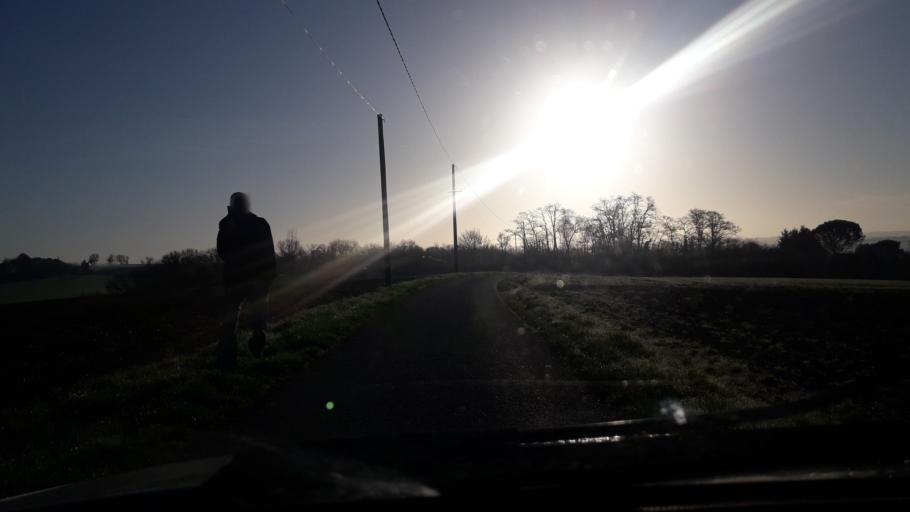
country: FR
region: Midi-Pyrenees
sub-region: Departement du Gers
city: Gimont
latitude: 43.6354
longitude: 0.9933
